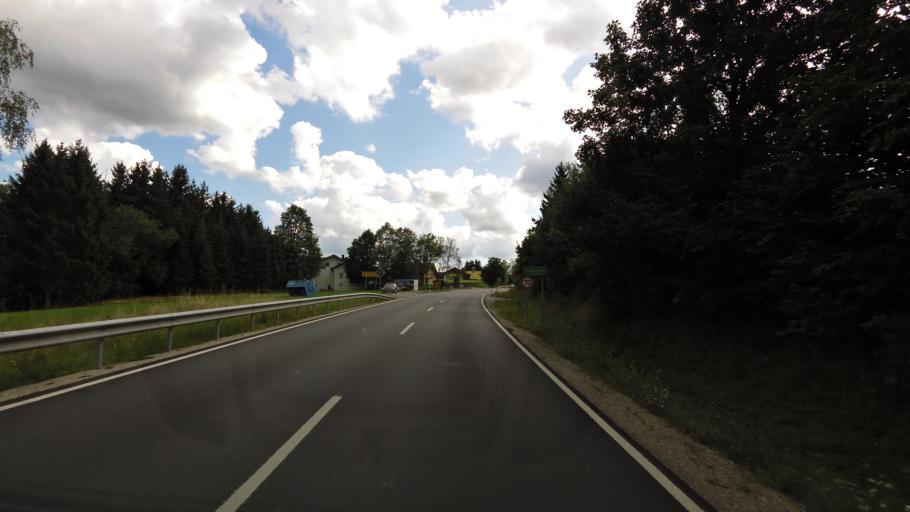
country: DE
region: Bavaria
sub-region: Upper Palatinate
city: Traitsching
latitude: 49.1290
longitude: 12.6531
